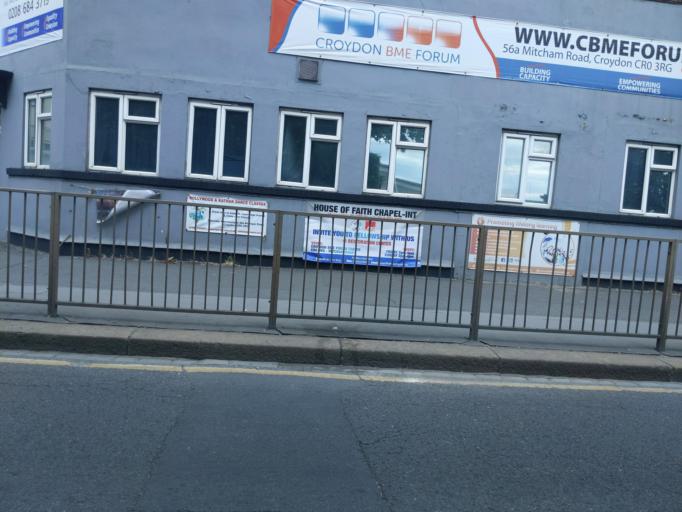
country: GB
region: England
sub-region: Greater London
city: Croydon
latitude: 51.3785
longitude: -0.1098
